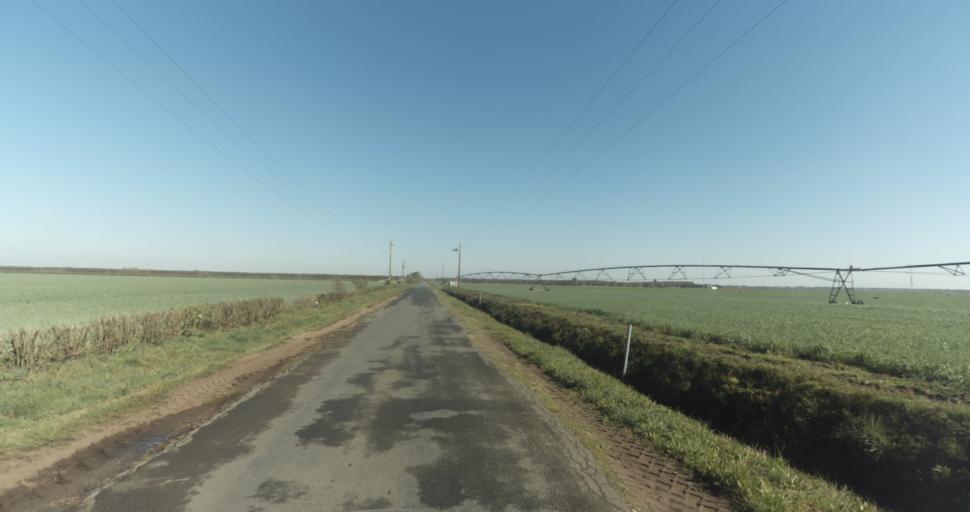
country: FR
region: Aquitaine
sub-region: Departement de la Gironde
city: Marcheprime
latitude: 44.7682
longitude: -0.8557
